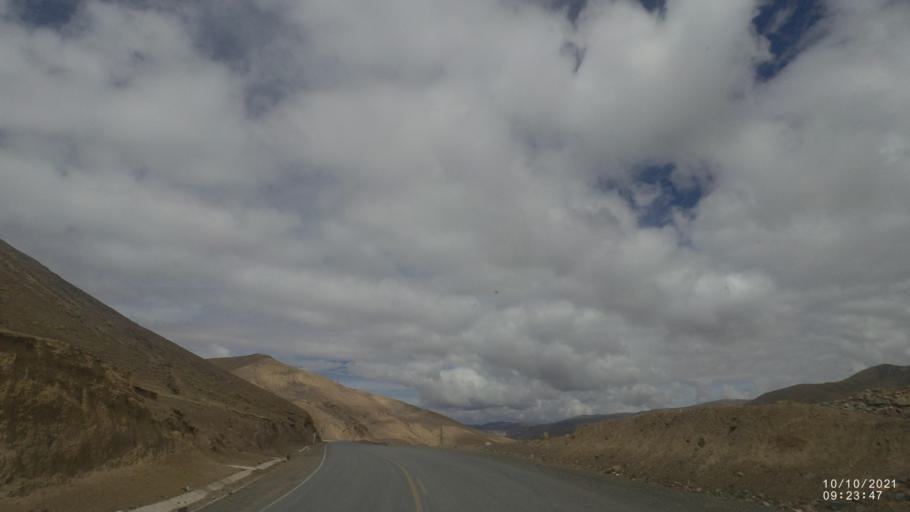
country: BO
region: La Paz
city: Quime
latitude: -17.0866
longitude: -67.3055
